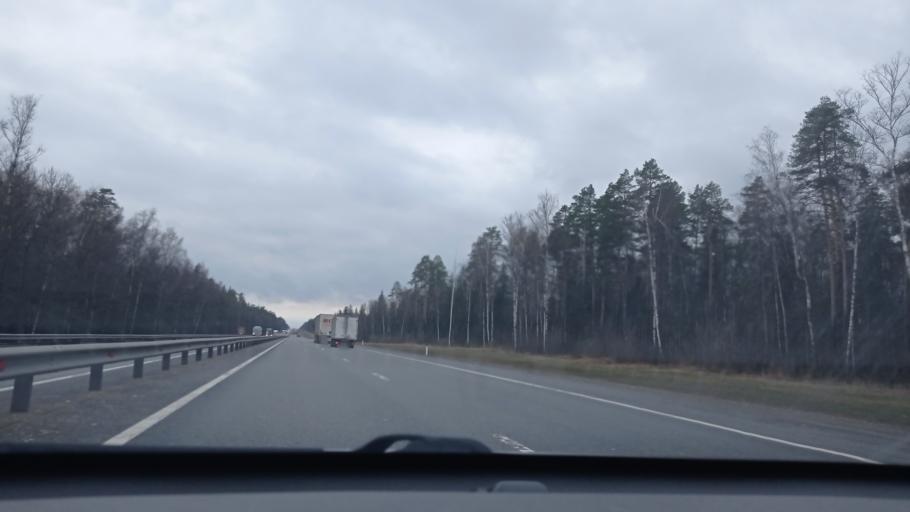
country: RU
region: Vladimir
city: Lakinsk
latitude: 55.9914
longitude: 39.8742
